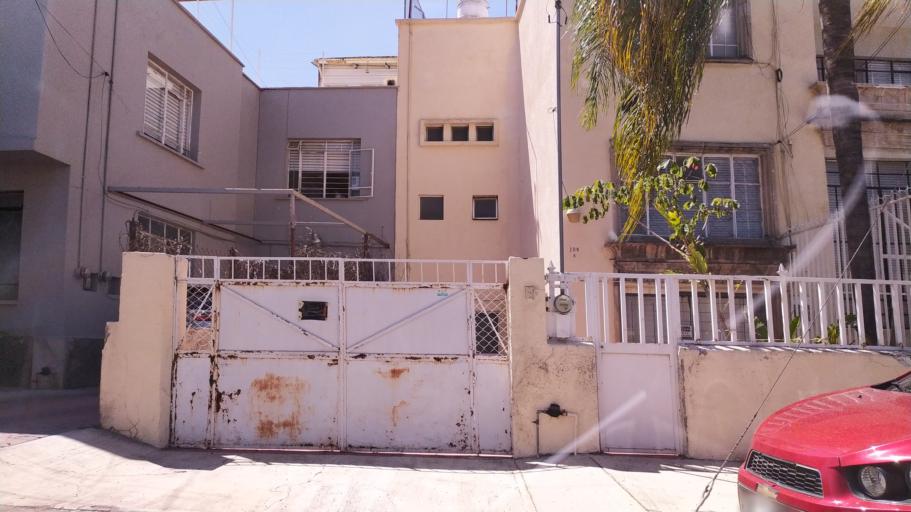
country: MX
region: Jalisco
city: Guadalajara
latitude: 20.6722
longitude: -103.3905
